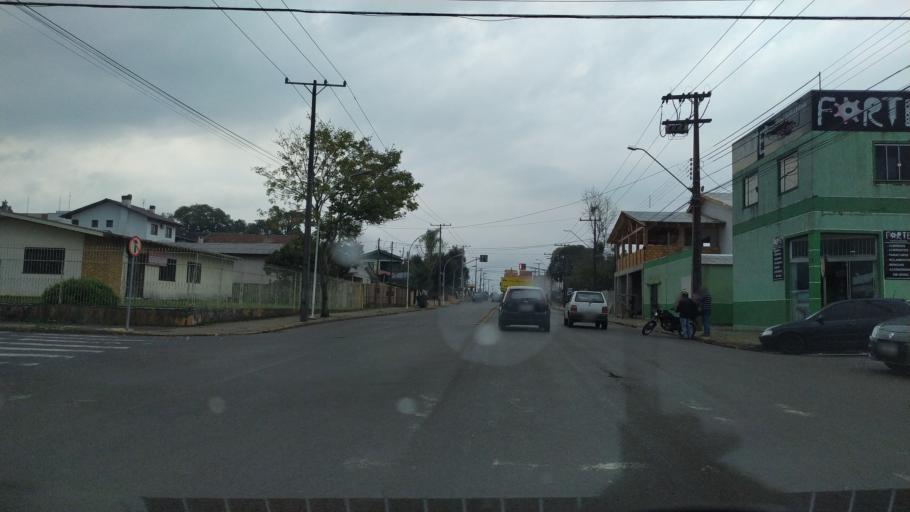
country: BR
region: Parana
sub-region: Palmas
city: Palmas
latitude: -26.4835
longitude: -51.9969
